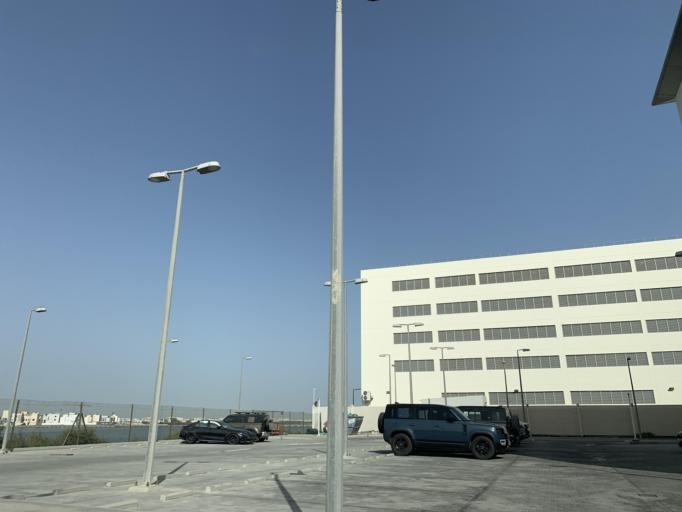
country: BH
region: Northern
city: Sitrah
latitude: 26.1526
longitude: 50.6092
